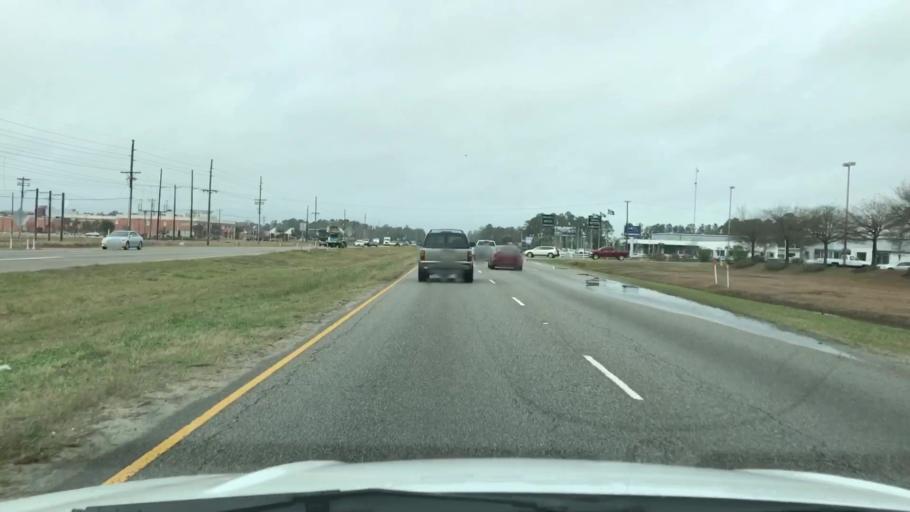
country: US
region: South Carolina
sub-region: Horry County
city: Red Hill
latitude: 33.7917
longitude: -78.9977
